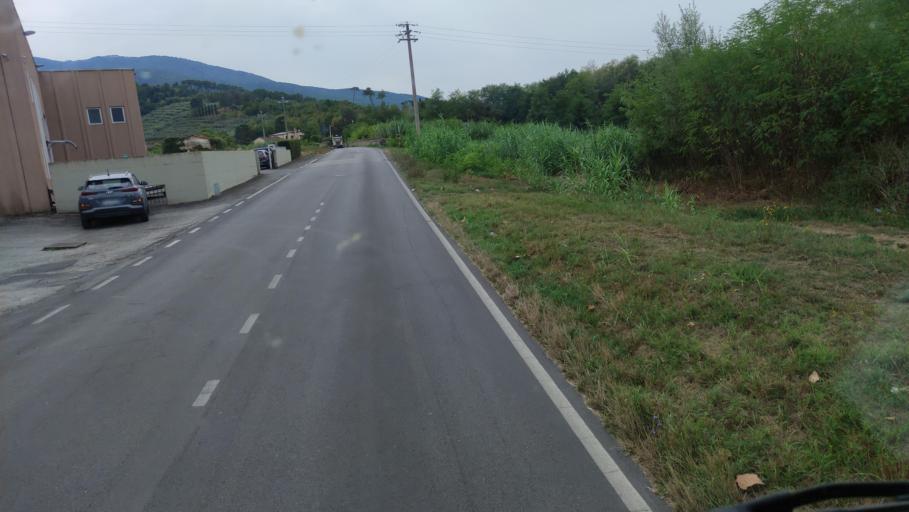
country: IT
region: Tuscany
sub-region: Provincia di Lucca
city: Lucca
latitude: 43.8057
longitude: 10.4972
